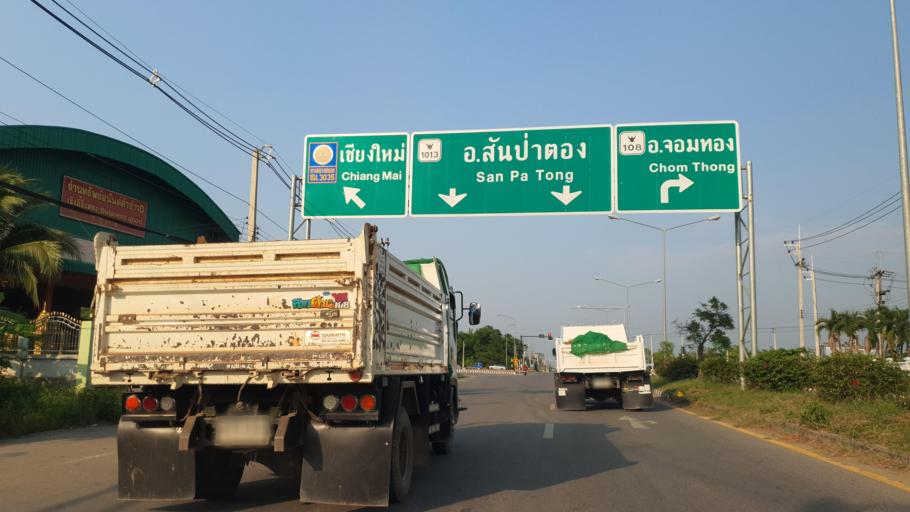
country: TH
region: Chiang Mai
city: Mae Wang
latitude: 18.6051
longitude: 98.8335
